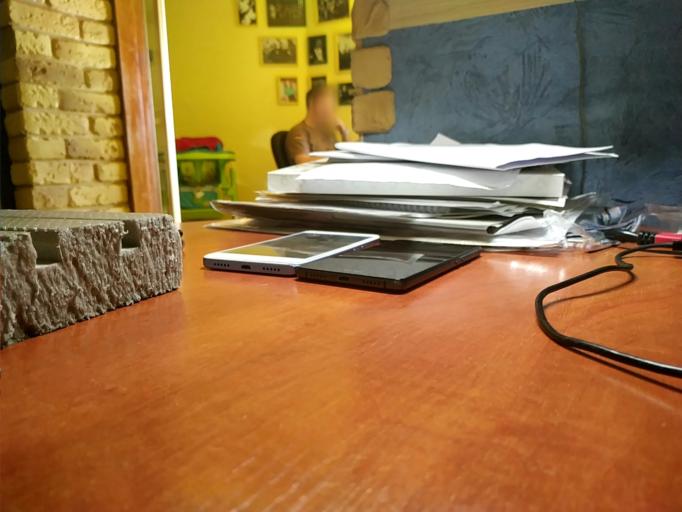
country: RU
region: Vologda
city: Nelazskoye
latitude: 59.4946
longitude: 37.6044
